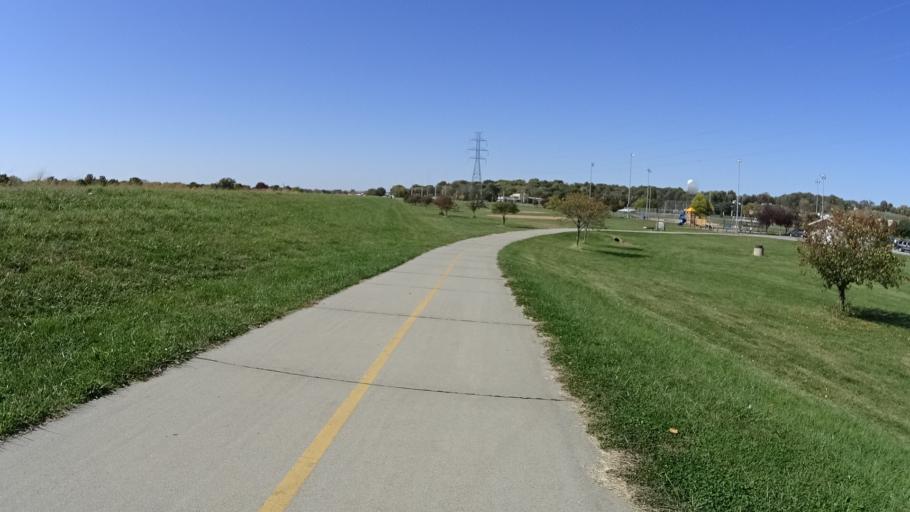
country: US
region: Nebraska
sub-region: Sarpy County
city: Papillion
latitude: 41.1545
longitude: -96.0270
